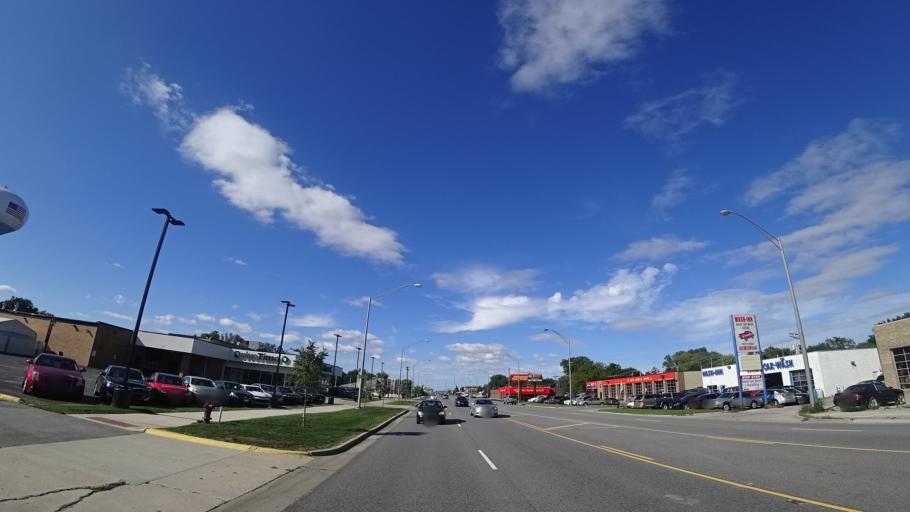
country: US
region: Illinois
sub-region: Cook County
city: Midlothian
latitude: 41.6280
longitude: -87.7375
